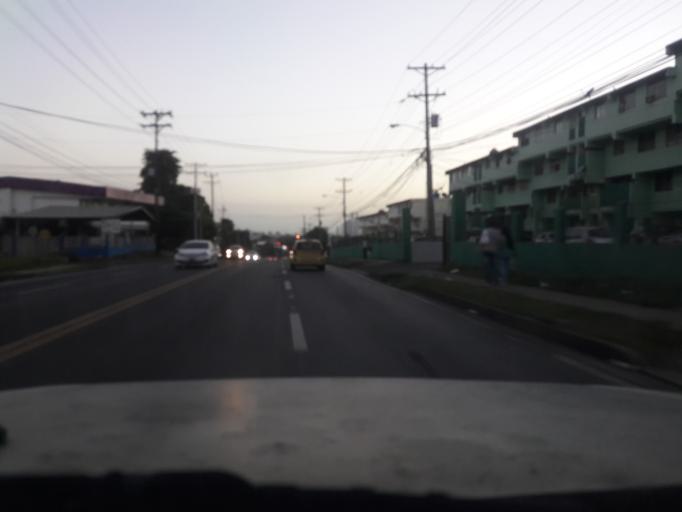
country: PA
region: Panama
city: San Miguelito
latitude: 9.0540
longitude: -79.4349
